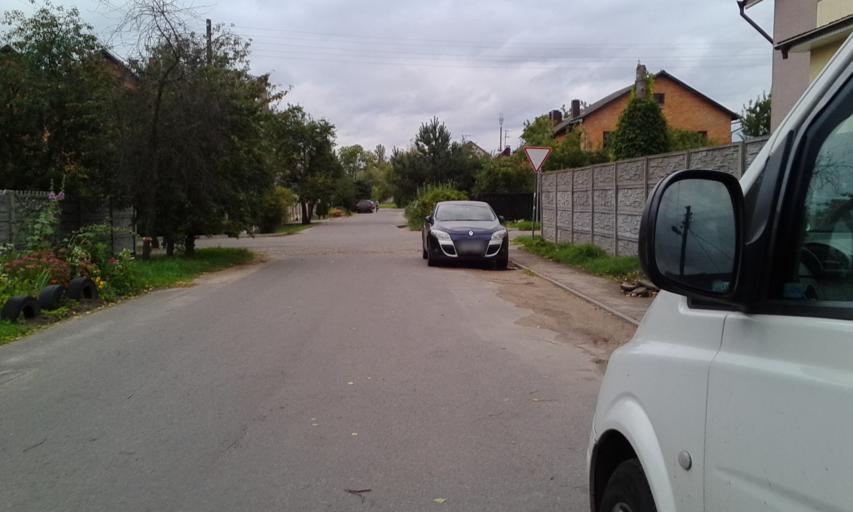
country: BY
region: Minsk
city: Minsk
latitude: 53.9461
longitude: 27.5877
